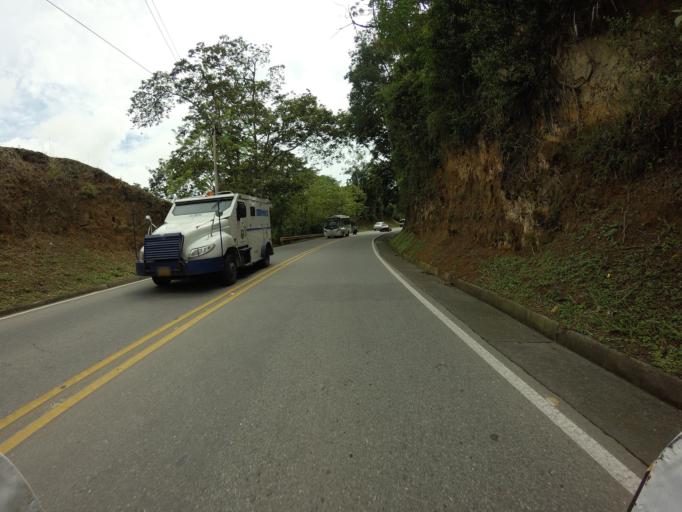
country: CO
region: Quindio
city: Quimbaya
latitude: 4.6008
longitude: -75.7791
